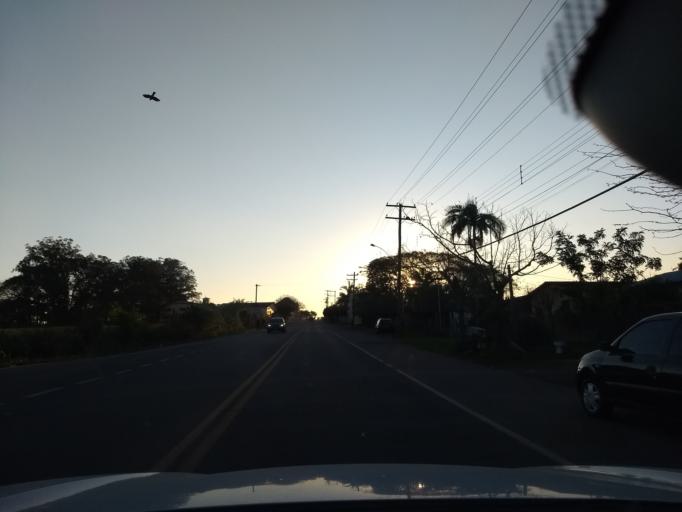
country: BR
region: Rio Grande do Sul
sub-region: Santa Cruz Do Sul
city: Santa Cruz do Sul
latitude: -29.7206
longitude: -52.5188
